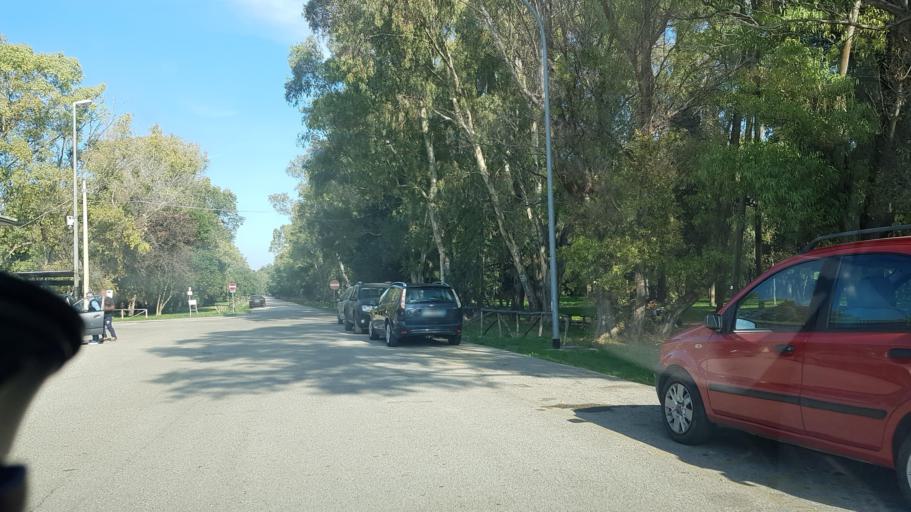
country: IT
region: Apulia
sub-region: Provincia di Foggia
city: Carapelle
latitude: 41.3838
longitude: 15.6431
